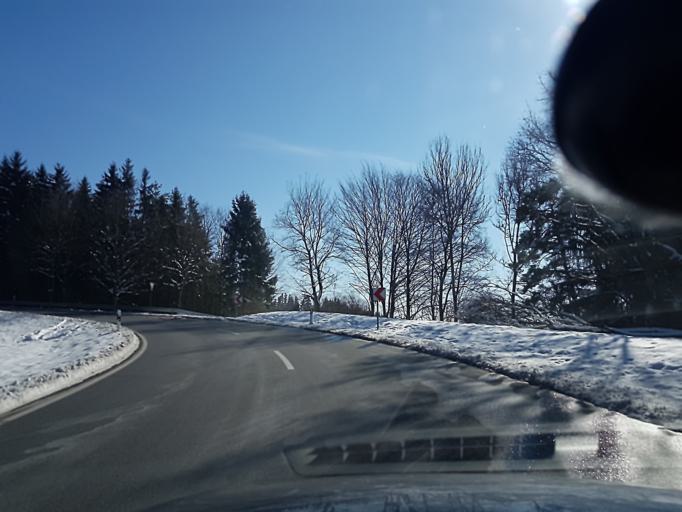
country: DE
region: Baden-Wuerttemberg
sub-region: Freiburg Region
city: Niedereschach
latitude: 48.1670
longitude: 8.5462
